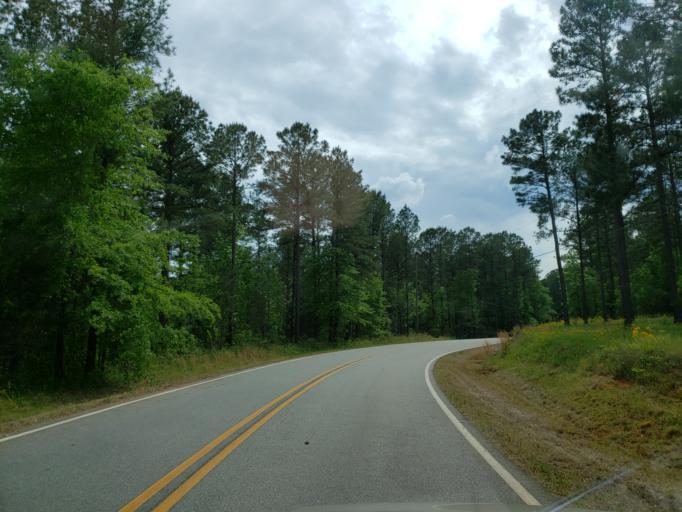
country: US
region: Georgia
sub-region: Monroe County
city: Forsyth
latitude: 32.9444
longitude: -83.9344
